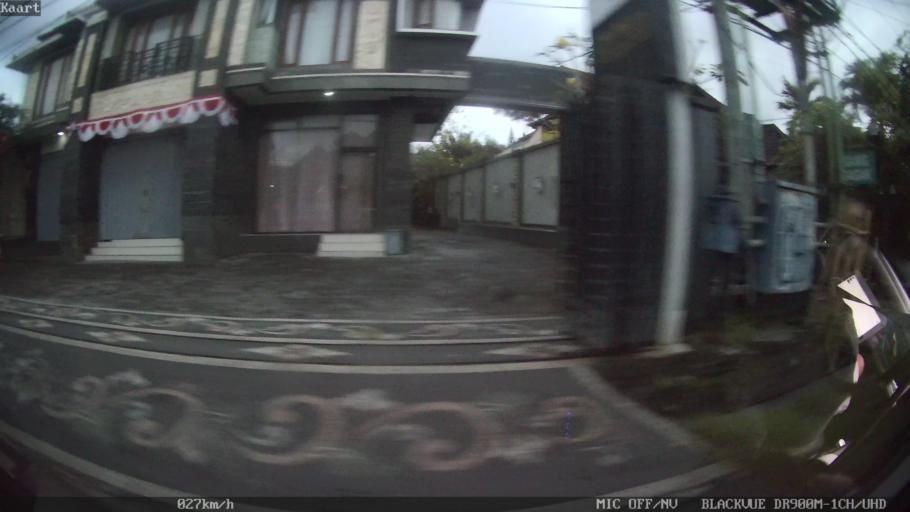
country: ID
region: Bali
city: Banjar Kertajiwa
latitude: -8.6262
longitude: 115.2675
